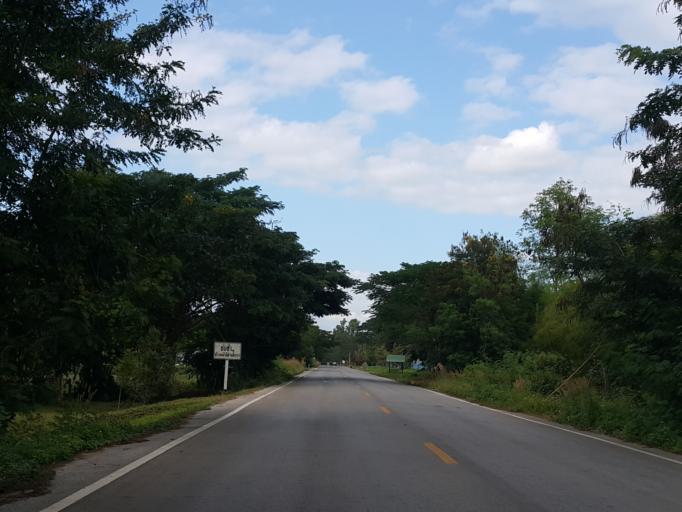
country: TH
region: Lampang
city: Chae Hom
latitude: 18.6460
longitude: 99.4940
